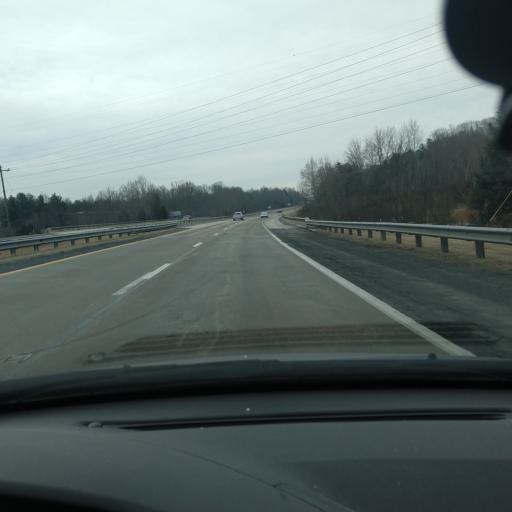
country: US
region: North Carolina
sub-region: Davidson County
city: Midway
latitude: 36.0161
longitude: -80.2355
